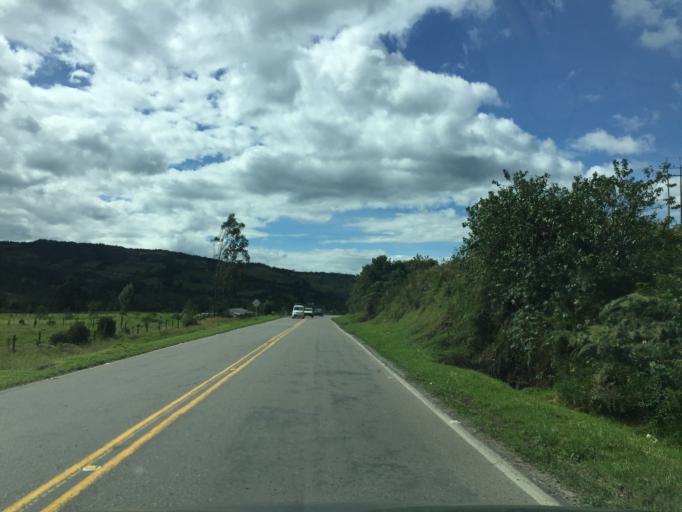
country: CO
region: Boyaca
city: Arcabuco
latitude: 5.7710
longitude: -73.4559
